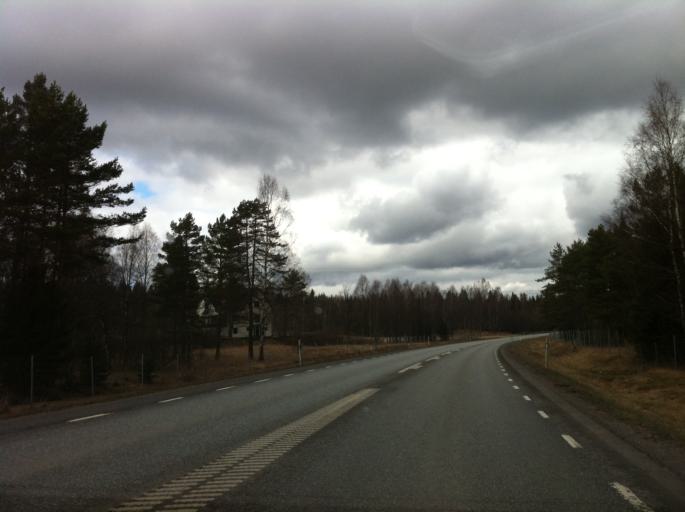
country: SE
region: Vaestra Goetaland
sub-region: Tranemo Kommun
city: Tranemo
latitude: 57.4579
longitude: 13.3197
